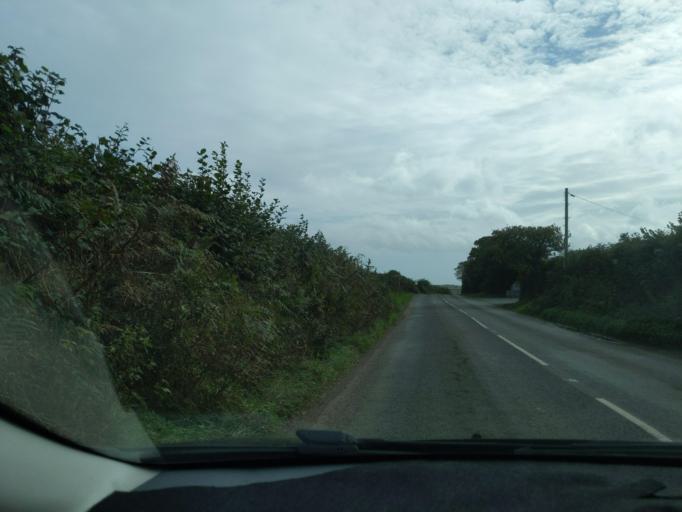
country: GB
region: England
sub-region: Cornwall
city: Mevagissey
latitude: 50.2607
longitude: -4.8274
